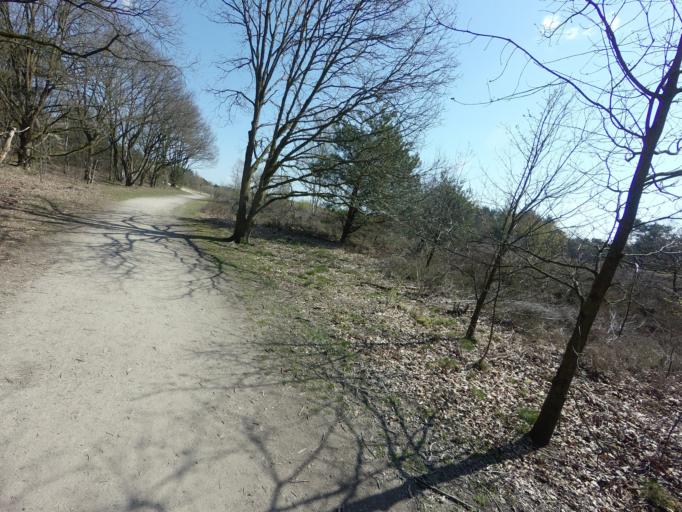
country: NL
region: Limburg
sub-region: Gemeente Bergen
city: Wellerlooi
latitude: 51.6078
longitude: 6.0618
